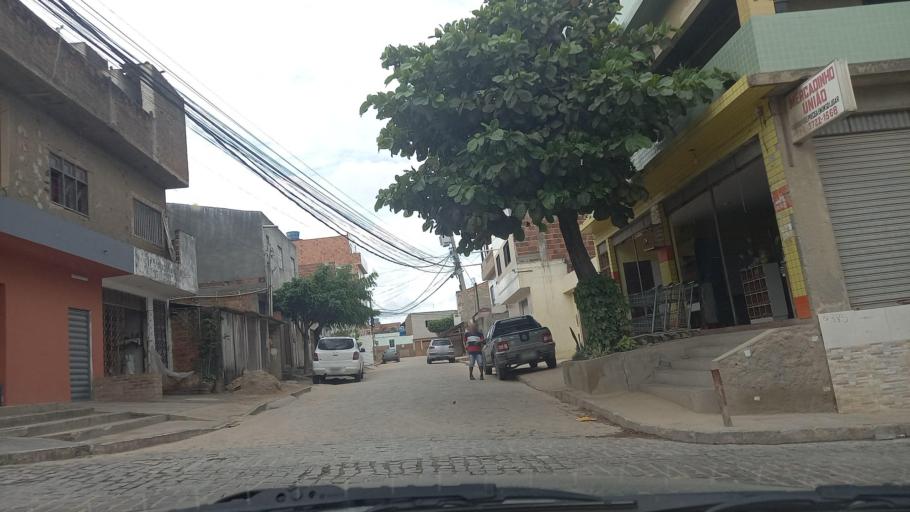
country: BR
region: Pernambuco
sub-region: Caruaru
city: Caruaru
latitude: -8.2675
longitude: -35.9564
